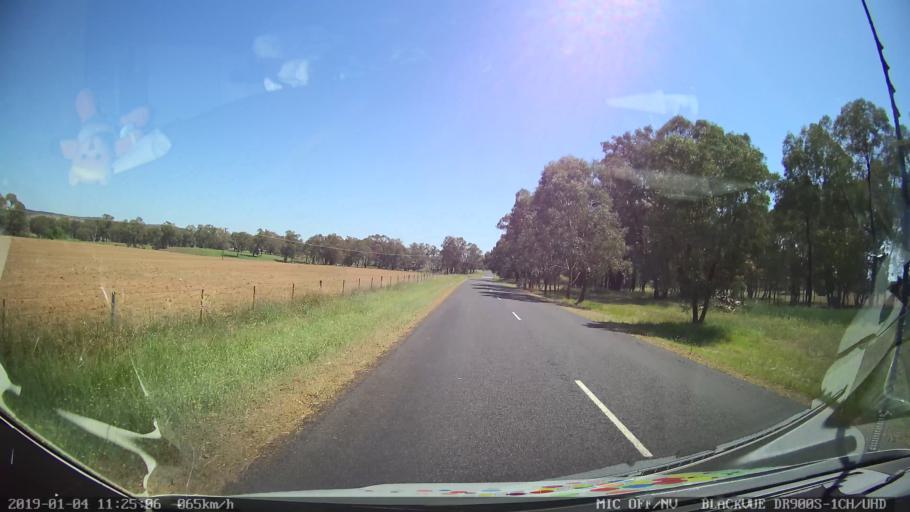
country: AU
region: New South Wales
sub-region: Cabonne
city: Molong
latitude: -33.1287
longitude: 148.7523
